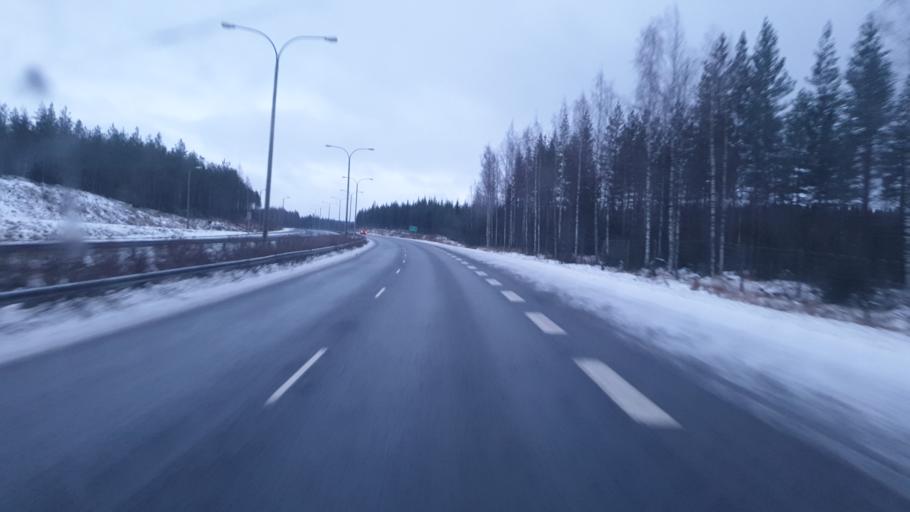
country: FI
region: Northern Savo
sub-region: Kuopio
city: Siilinjaervi
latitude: 63.0167
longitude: 27.6652
